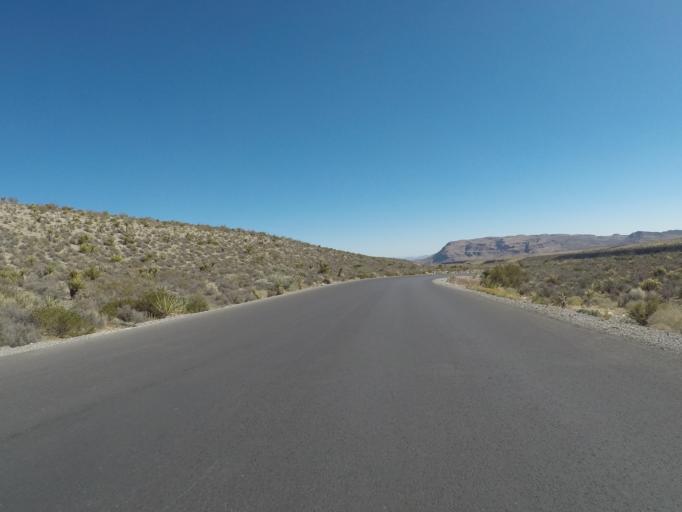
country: US
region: Nevada
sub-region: Clark County
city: Summerlin South
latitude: 36.1470
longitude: -115.4777
